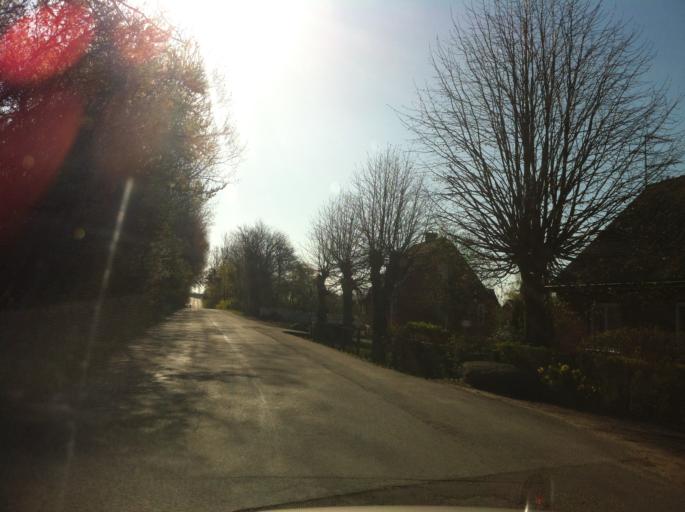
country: SE
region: Skane
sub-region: Svalovs Kommun
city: Teckomatorp
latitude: 55.8784
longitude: 13.0118
